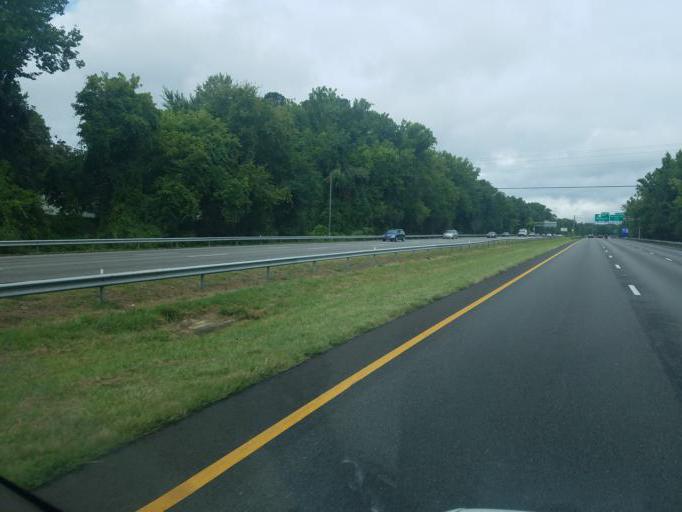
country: US
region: Virginia
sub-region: Henrico County
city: Chamberlayne
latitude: 37.6272
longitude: -77.4476
